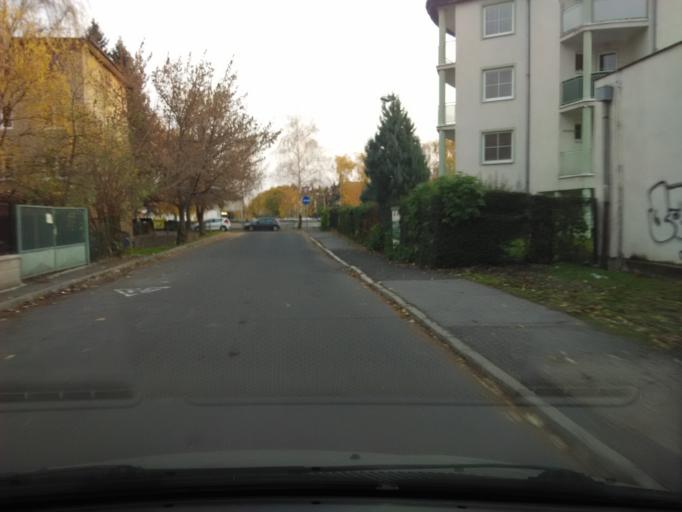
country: SK
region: Nitriansky
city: Levice
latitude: 48.2152
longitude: 18.5980
